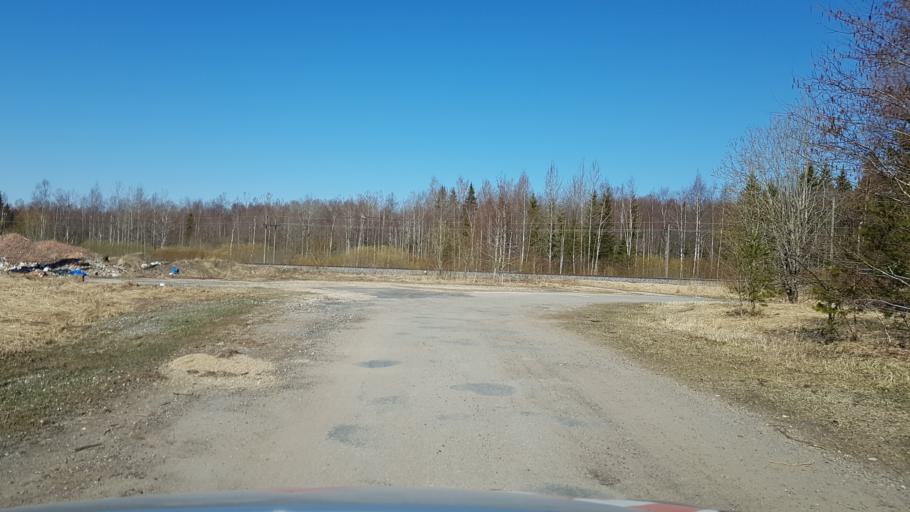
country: EE
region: Ida-Virumaa
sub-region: Kohtla-Nomme vald
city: Kohtla-Nomme
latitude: 59.3603
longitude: 27.1704
